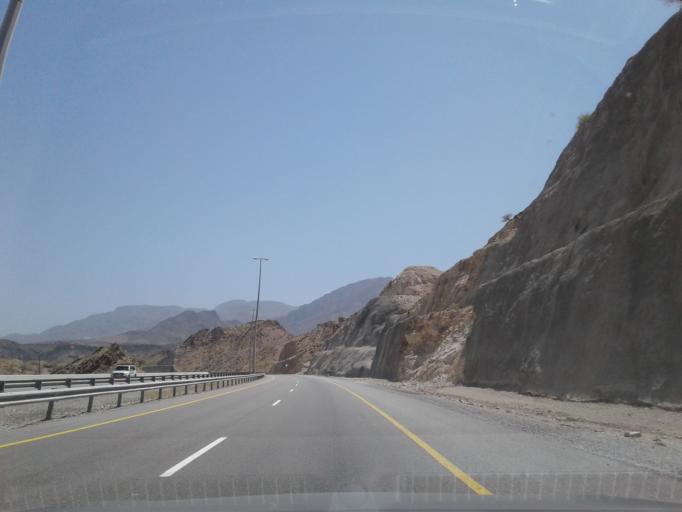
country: OM
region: Muhafazat Masqat
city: Muscat
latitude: 23.2167
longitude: 58.7952
